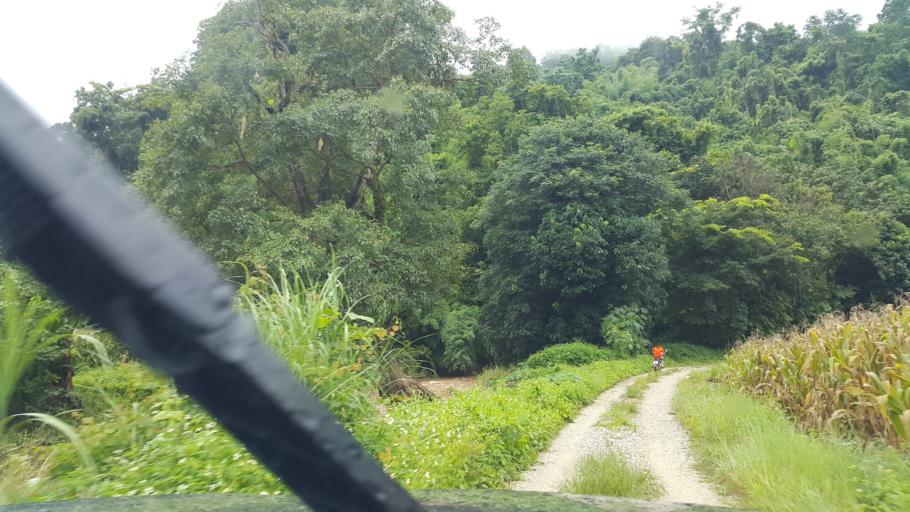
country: TH
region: Phayao
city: Chiang Kham
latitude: 19.4999
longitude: 100.4544
